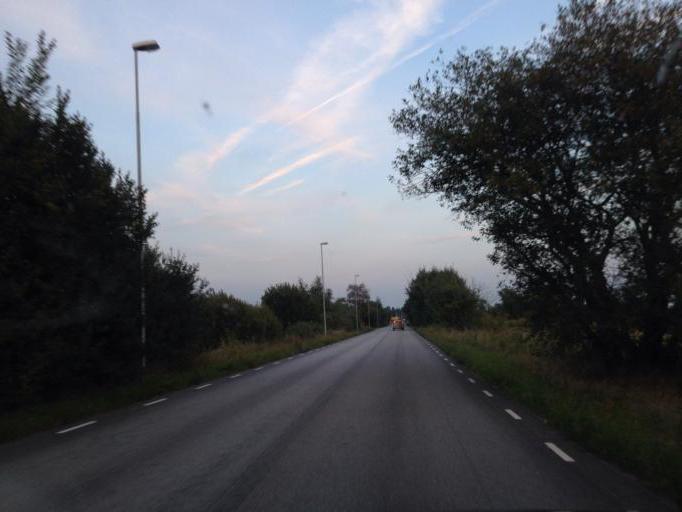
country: SE
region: Skane
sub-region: Lomma Kommun
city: Lomma
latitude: 55.6873
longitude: 13.0850
